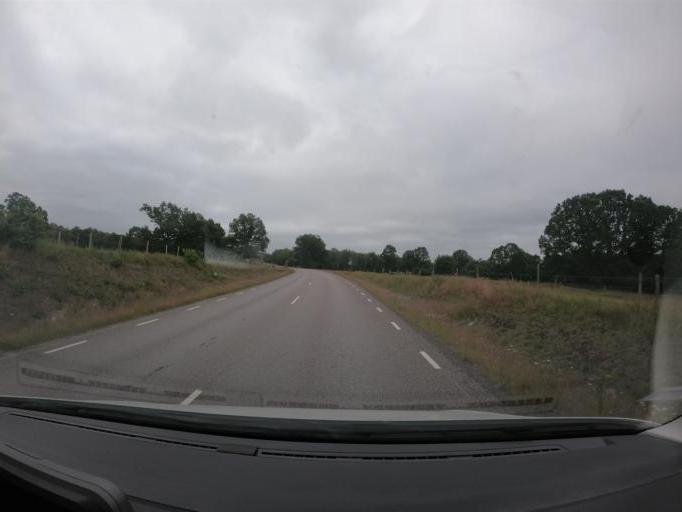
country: SE
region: Skane
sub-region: Perstorps Kommun
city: Perstorp
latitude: 56.1772
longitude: 13.3559
